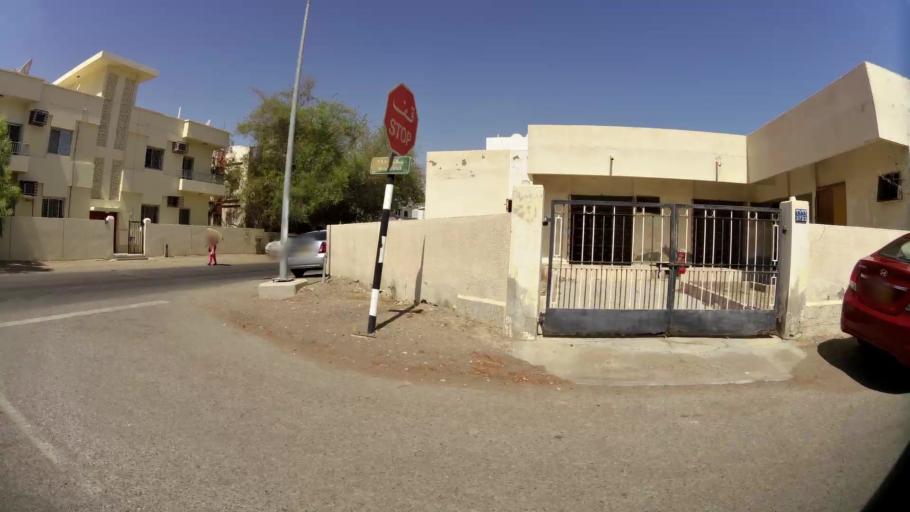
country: OM
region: Muhafazat Masqat
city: Muscat
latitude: 23.5999
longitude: 58.5445
